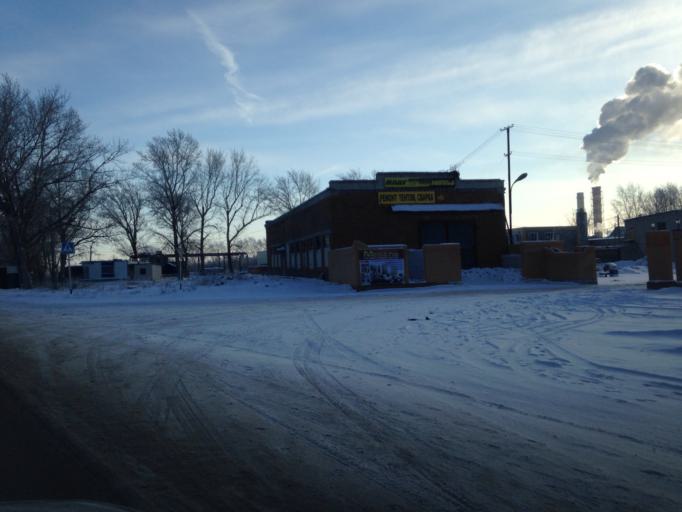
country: RU
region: Ulyanovsk
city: Novoul'yanovsk
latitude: 54.1636
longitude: 48.3586
